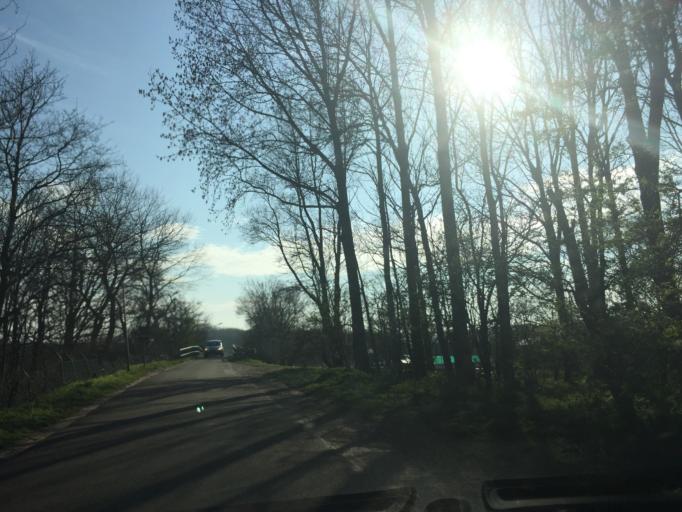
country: NL
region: South Holland
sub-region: Gemeente Noordwijkerhout
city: Noordwijkerhout
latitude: 52.2490
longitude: 4.4838
